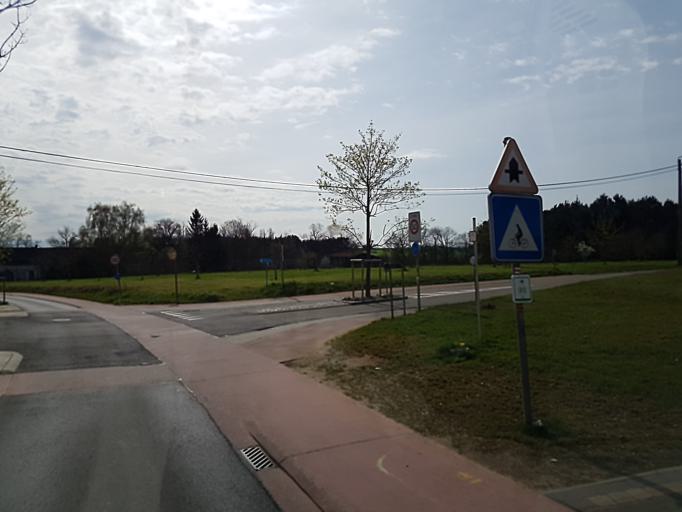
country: BE
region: Flanders
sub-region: Provincie Vlaams-Brabant
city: Scherpenheuvel-Zichem
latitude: 50.9972
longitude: 4.9919
